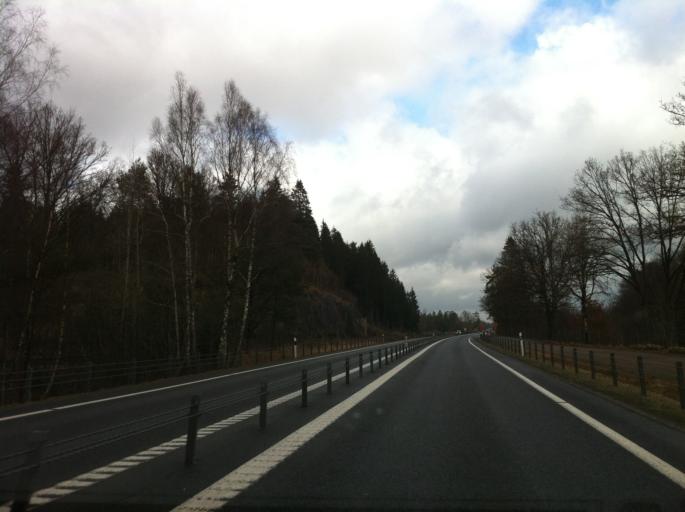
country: SE
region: Halland
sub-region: Halmstads Kommun
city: Oskarstrom
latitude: 56.8541
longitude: 13.0309
